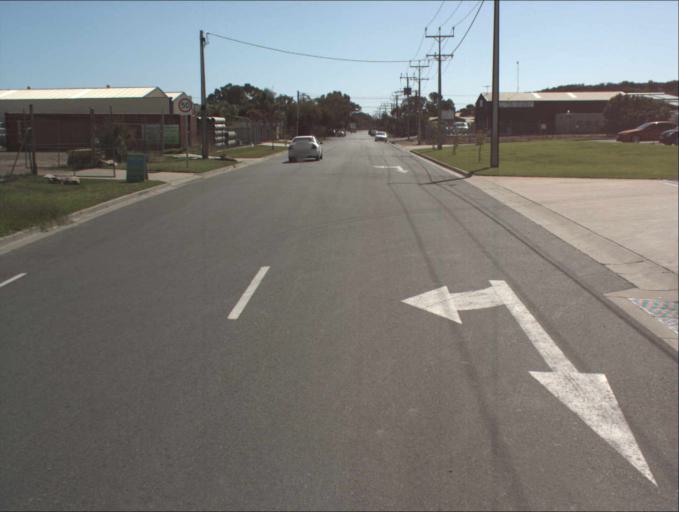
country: AU
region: South Australia
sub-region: Charles Sturt
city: Woodville North
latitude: -34.8366
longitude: 138.5626
